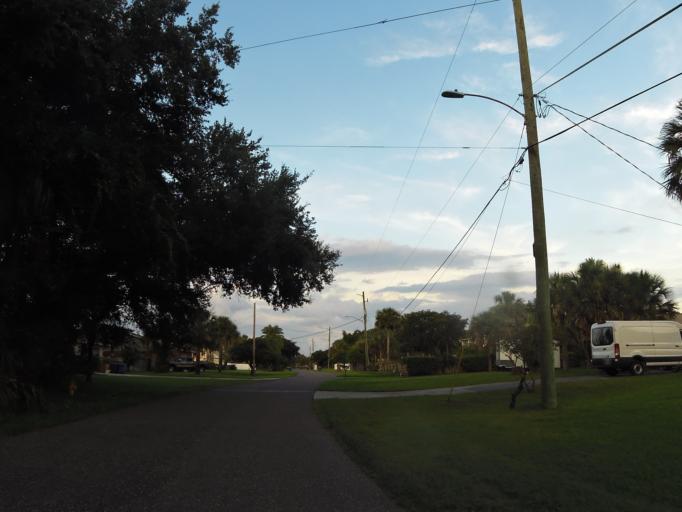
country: US
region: Florida
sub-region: Duval County
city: Atlantic Beach
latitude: 30.3935
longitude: -81.4991
